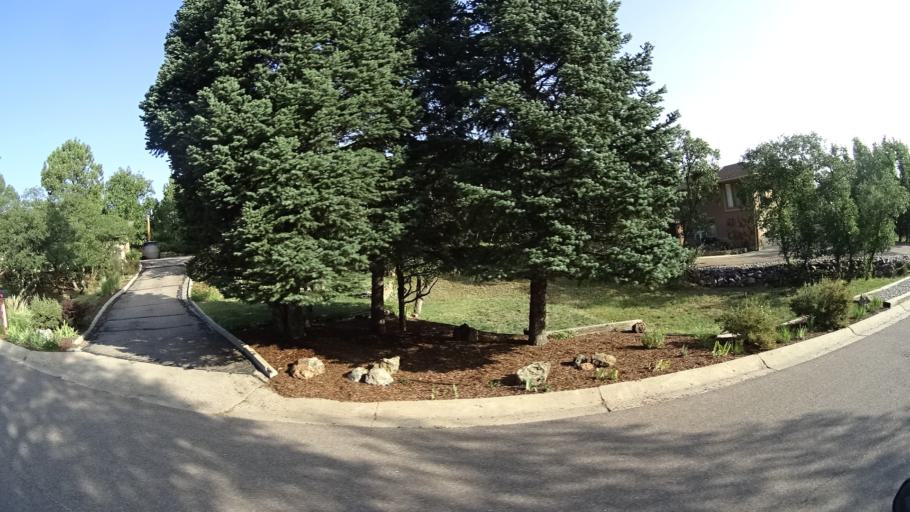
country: US
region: Colorado
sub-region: El Paso County
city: Colorado Springs
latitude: 38.8133
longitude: -104.8647
